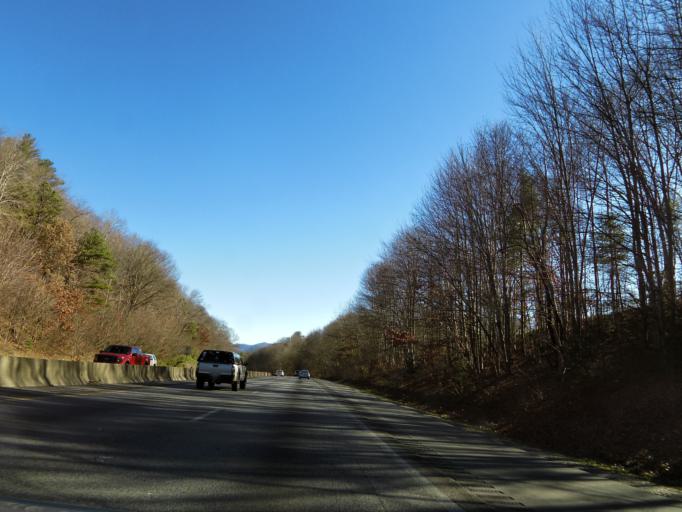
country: US
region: North Carolina
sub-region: Haywood County
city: Clyde
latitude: 35.5457
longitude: -82.9018
